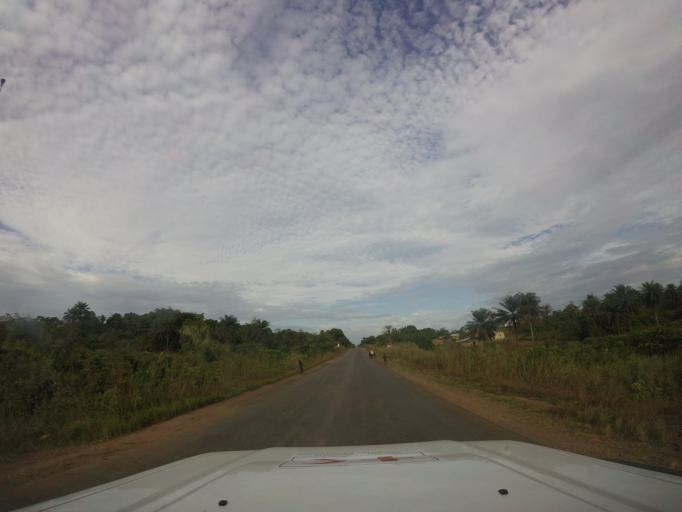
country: LR
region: Bomi
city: Tubmanburg
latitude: 6.7315
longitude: -11.0009
